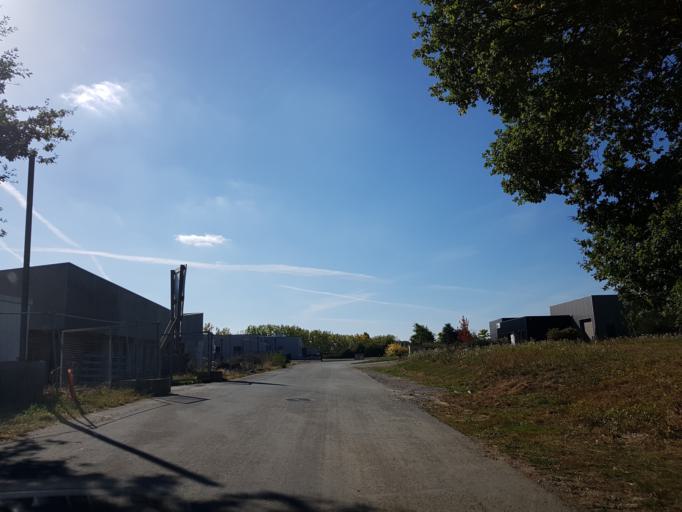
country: FR
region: Brittany
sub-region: Departement d'Ille-et-Vilaine
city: Chateaubourg
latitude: 48.1015
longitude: -1.4088
